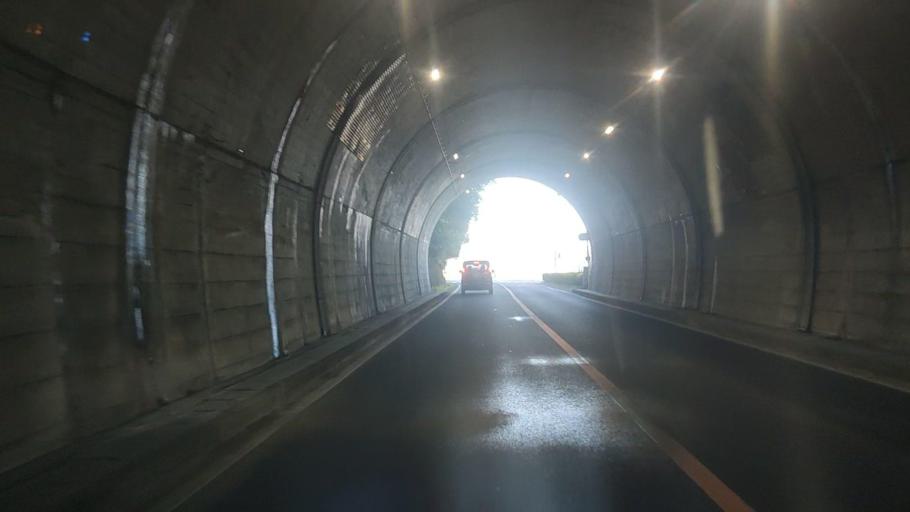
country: JP
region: Oita
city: Saiki
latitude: 32.9427
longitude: 131.9086
